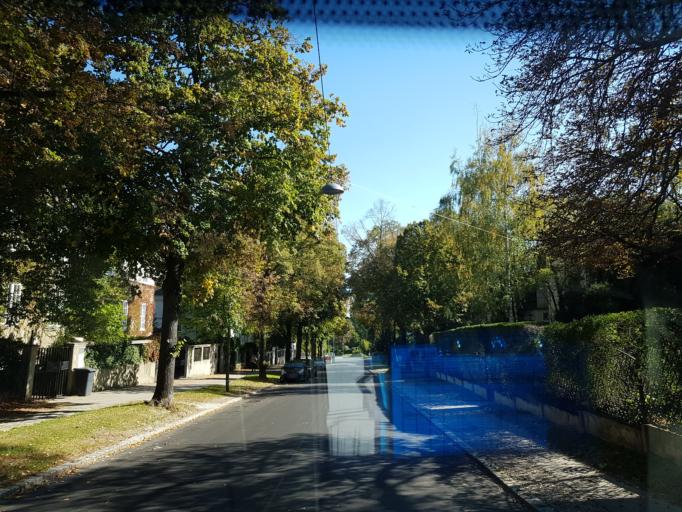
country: AT
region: Lower Austria
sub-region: Politischer Bezirk Korneuburg
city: Langenzersdorf
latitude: 48.2511
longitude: 16.3355
